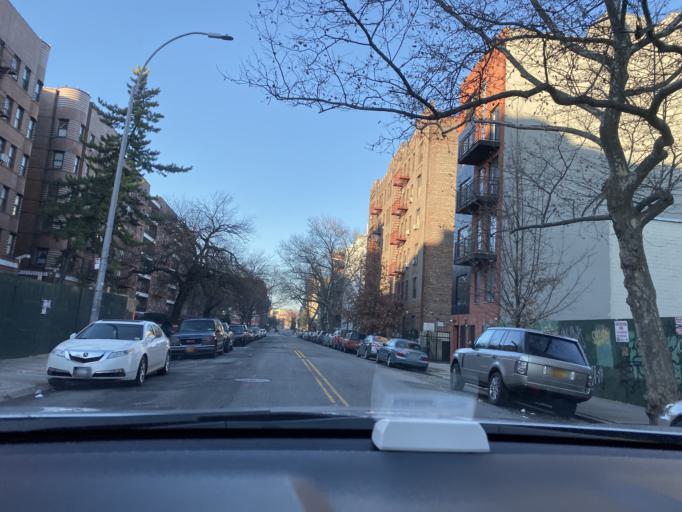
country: US
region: New York
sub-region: Kings County
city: Brooklyn
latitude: 40.6552
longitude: -73.9544
